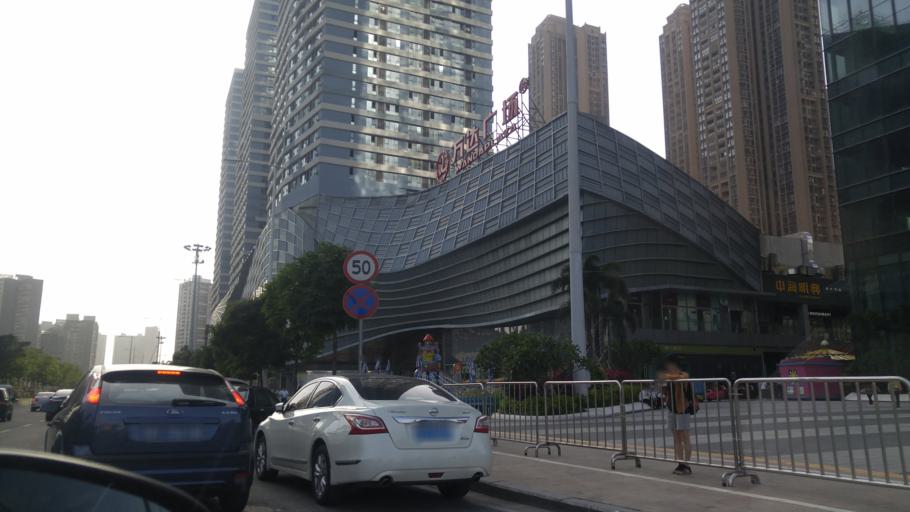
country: CN
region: Guangdong
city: Guicheng
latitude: 23.0659
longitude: 113.1540
